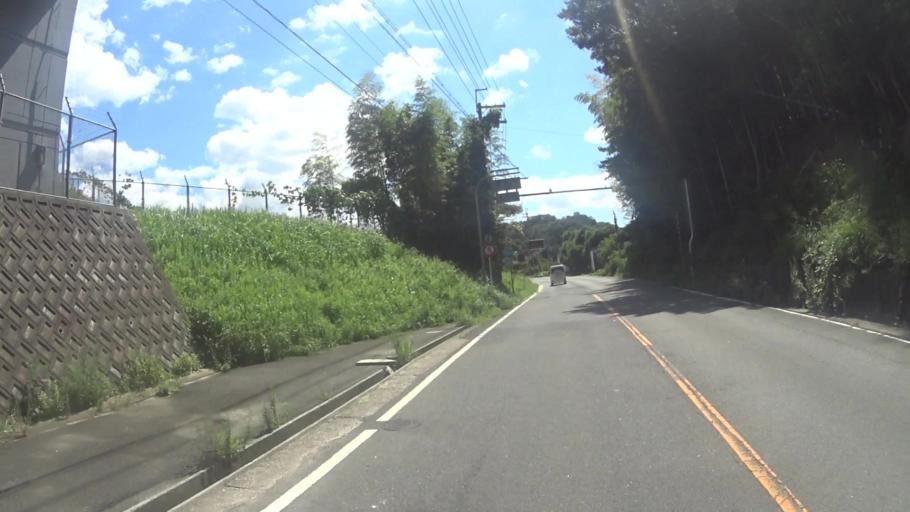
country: JP
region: Nara
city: Nara-shi
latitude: 34.7129
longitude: 135.8286
